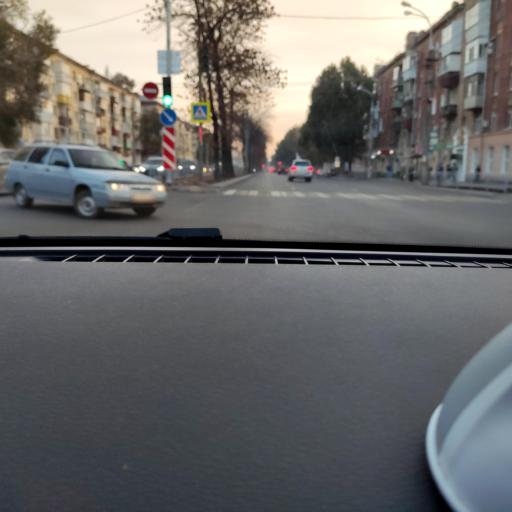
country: RU
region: Samara
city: Samara
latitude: 53.2085
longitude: 50.2391
